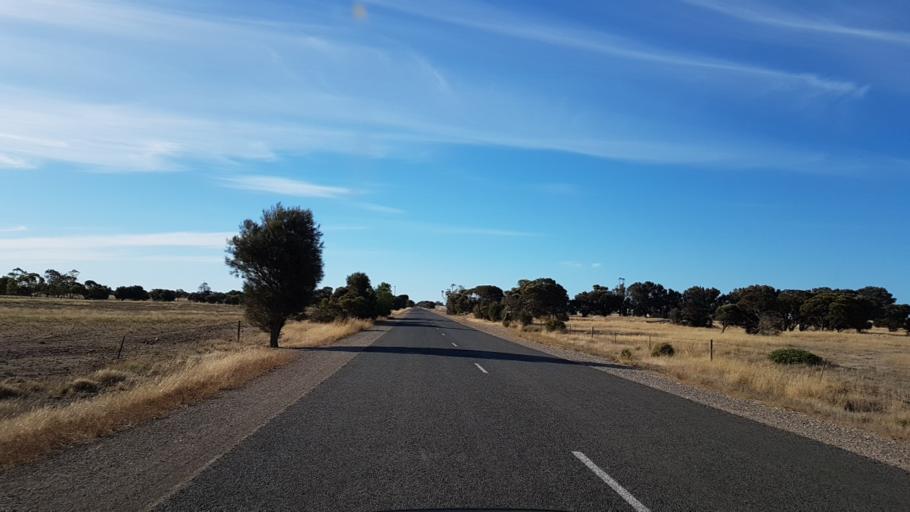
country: AU
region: South Australia
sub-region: Yorke Peninsula
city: Honiton
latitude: -34.9422
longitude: 137.0939
